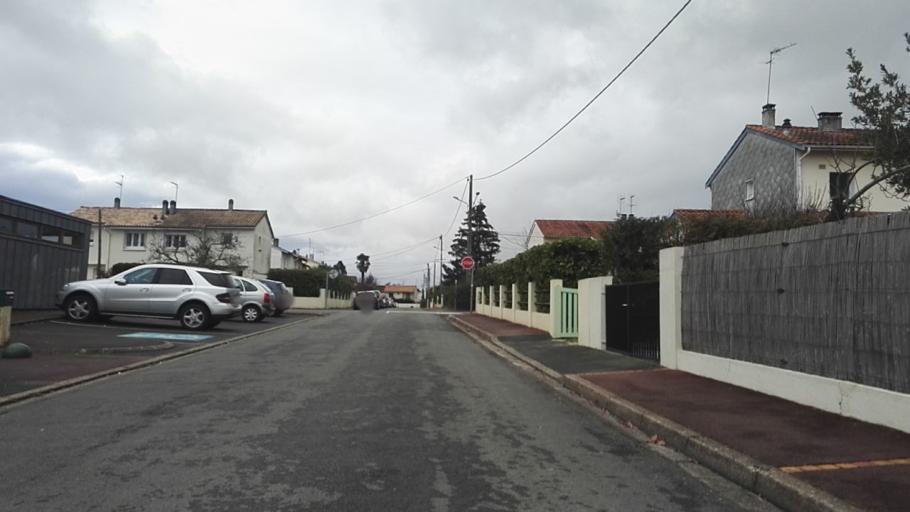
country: FR
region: Aquitaine
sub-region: Departement de la Gironde
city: Eysines
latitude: 44.8687
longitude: -0.6334
